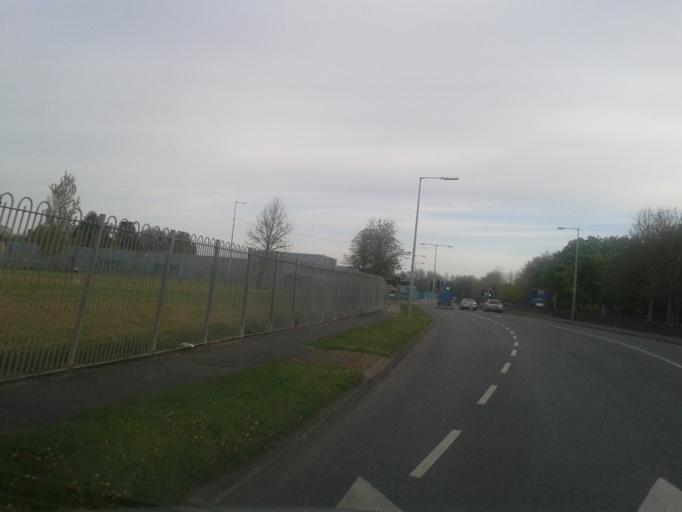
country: IE
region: Leinster
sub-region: Fingal County
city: Swords
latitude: 53.4674
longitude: -6.2194
